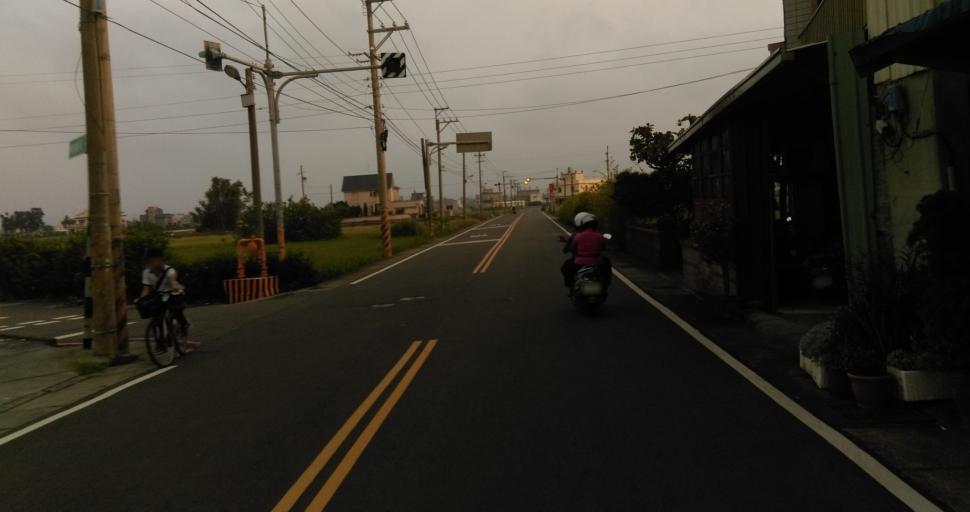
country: TW
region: Taiwan
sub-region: Hsinchu
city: Zhubei
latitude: 24.8735
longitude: 120.9564
